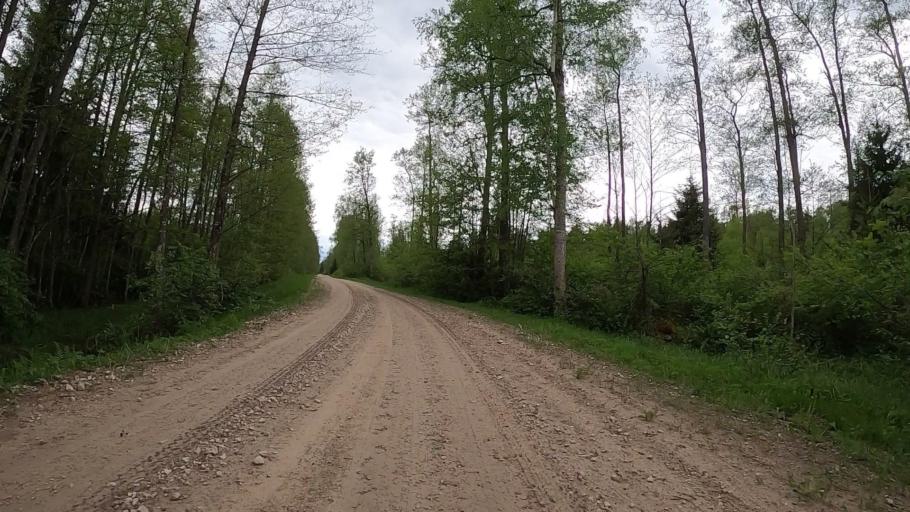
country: LV
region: Ozolnieku
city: Ozolnieki
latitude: 56.7849
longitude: 23.7699
